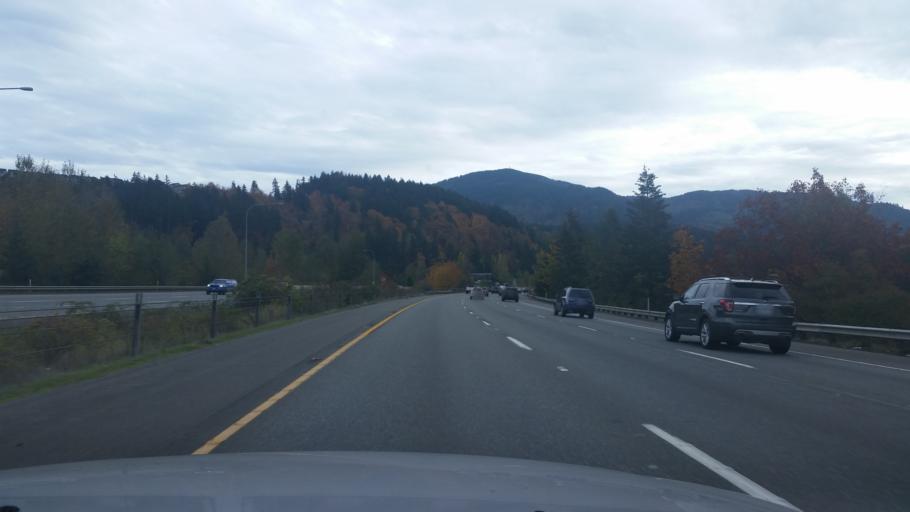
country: US
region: Washington
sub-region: King County
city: Issaquah
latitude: 47.5416
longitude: -122.0383
